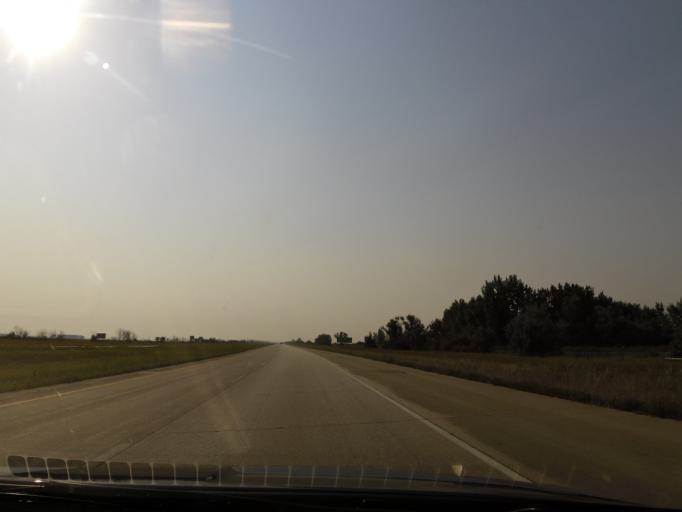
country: US
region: North Dakota
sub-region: Grand Forks County
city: Grand Forks
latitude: 48.0669
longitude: -97.1669
